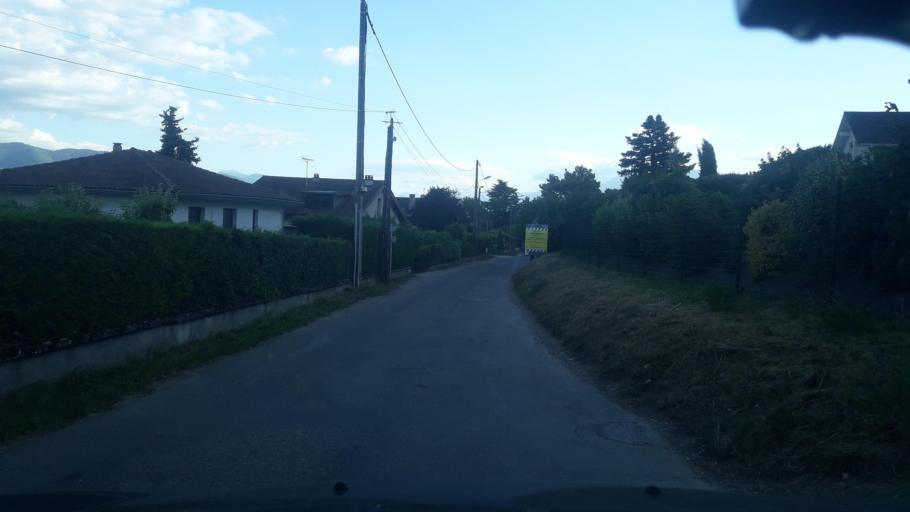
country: FR
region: Rhone-Alpes
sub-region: Departement de l'Isere
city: Biviers
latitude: 45.2323
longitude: 5.7988
